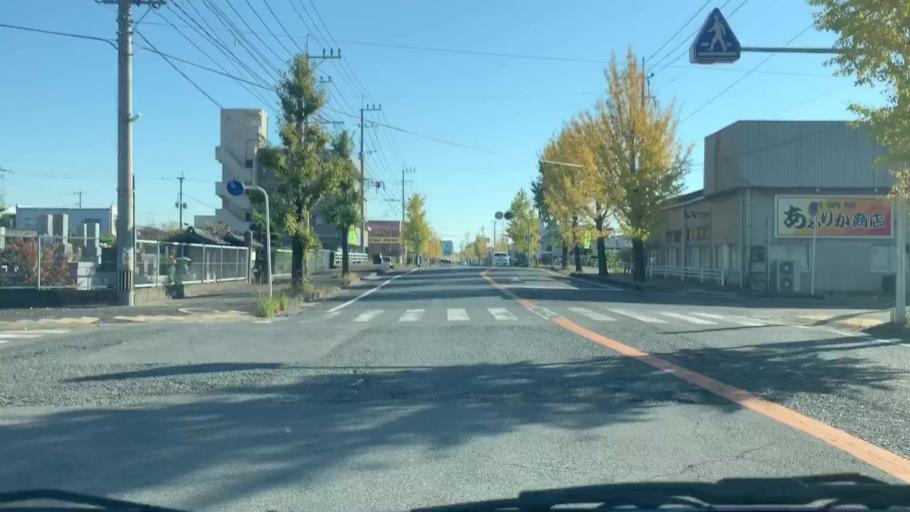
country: JP
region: Saga Prefecture
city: Saga-shi
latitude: 33.2559
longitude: 130.2673
